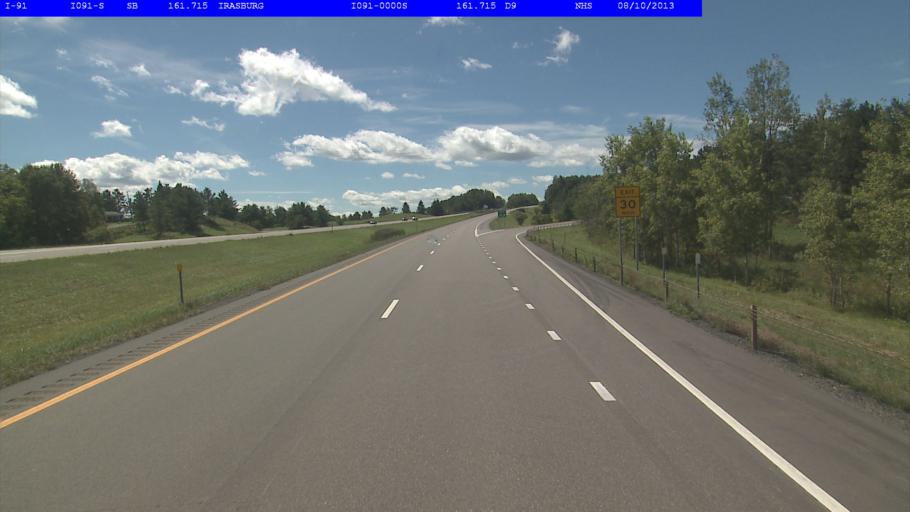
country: US
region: Vermont
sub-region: Orleans County
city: Newport
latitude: 44.8108
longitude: -72.2113
